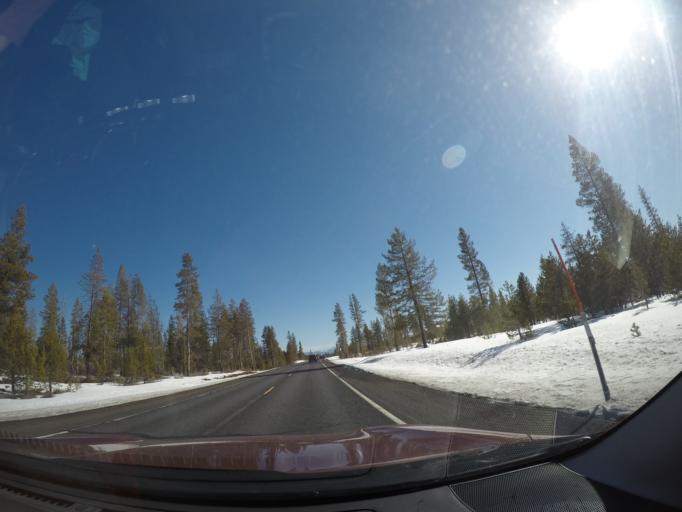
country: US
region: Oregon
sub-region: Deschutes County
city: Three Rivers
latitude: 43.8733
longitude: -121.5534
